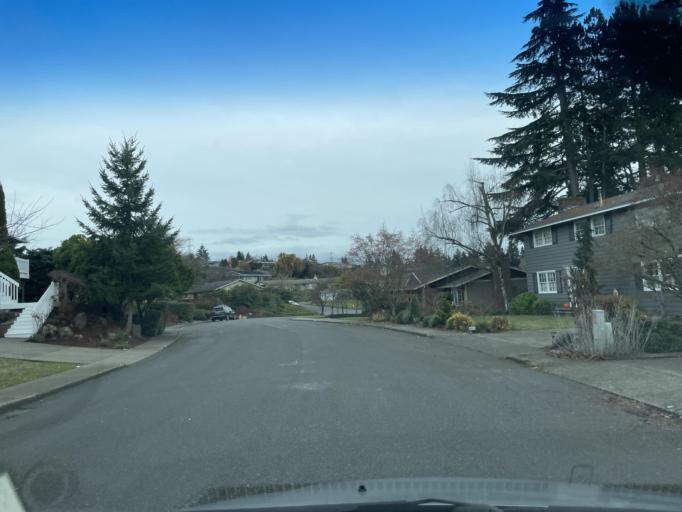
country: US
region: Washington
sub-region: King County
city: Newport
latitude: 47.5938
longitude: -122.1788
